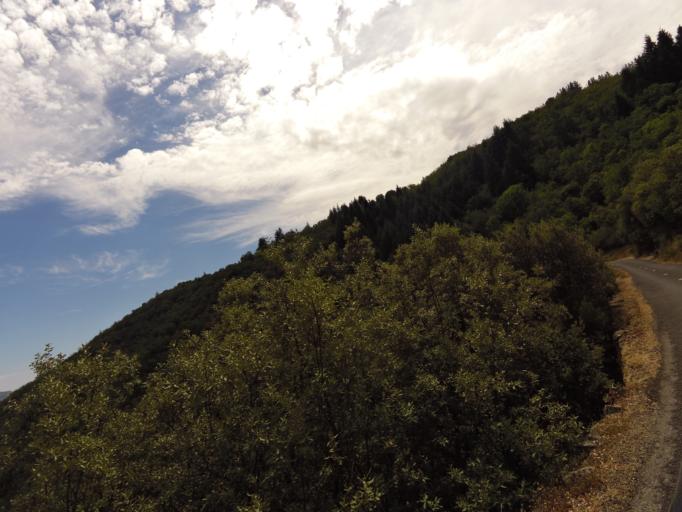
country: FR
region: Languedoc-Roussillon
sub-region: Departement du Gard
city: Le Vigan
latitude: 44.0198
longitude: 3.6358
